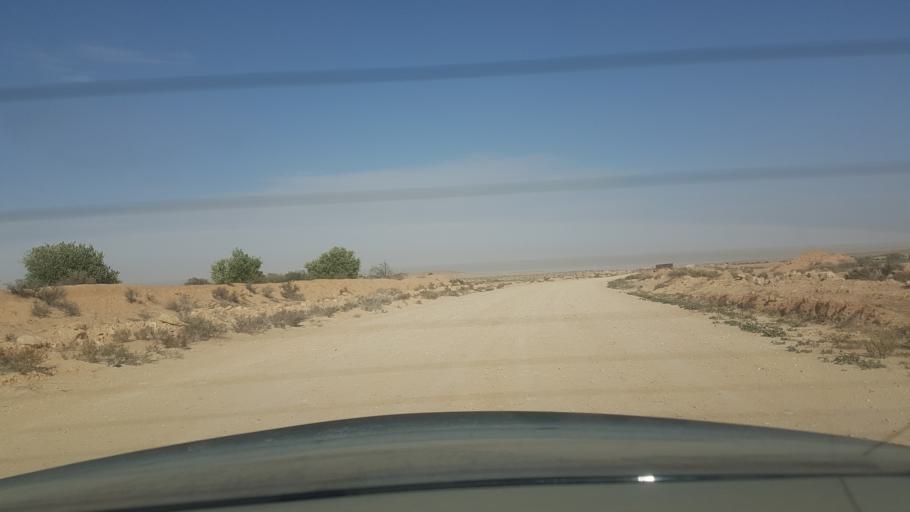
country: TN
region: Qabis
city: El Hamma
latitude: 33.6635
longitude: 9.7352
